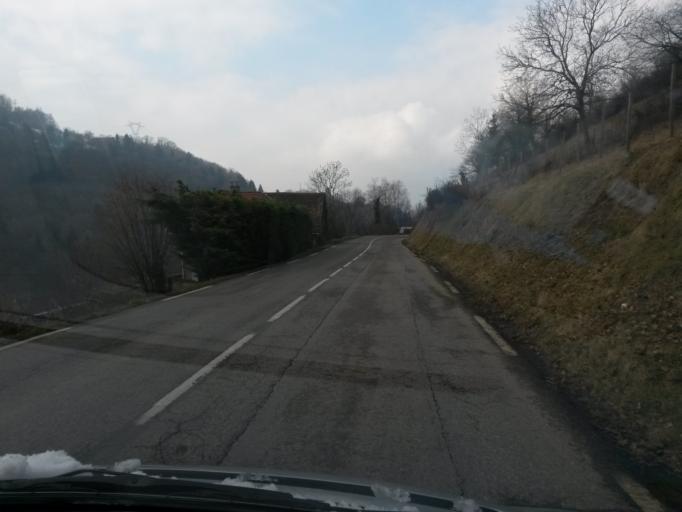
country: FR
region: Rhone-Alpes
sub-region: Departement de l'Isere
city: Tencin
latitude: 45.3045
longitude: 5.9750
